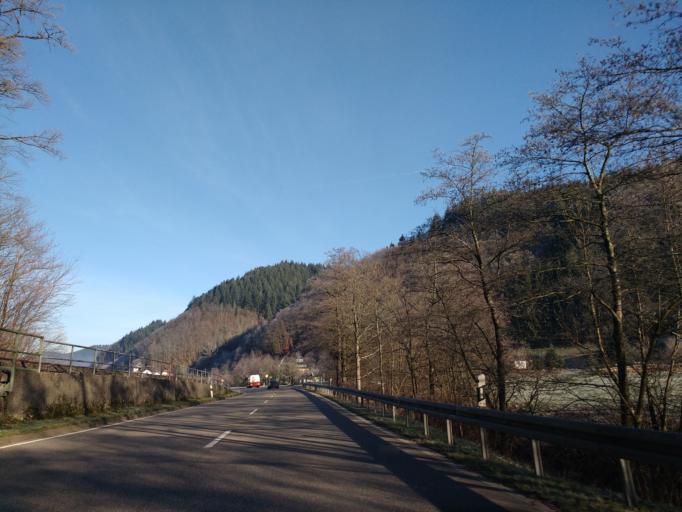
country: DE
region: Baden-Wuerttemberg
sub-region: Freiburg Region
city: Oppenau
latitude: 48.4515
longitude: 8.1638
